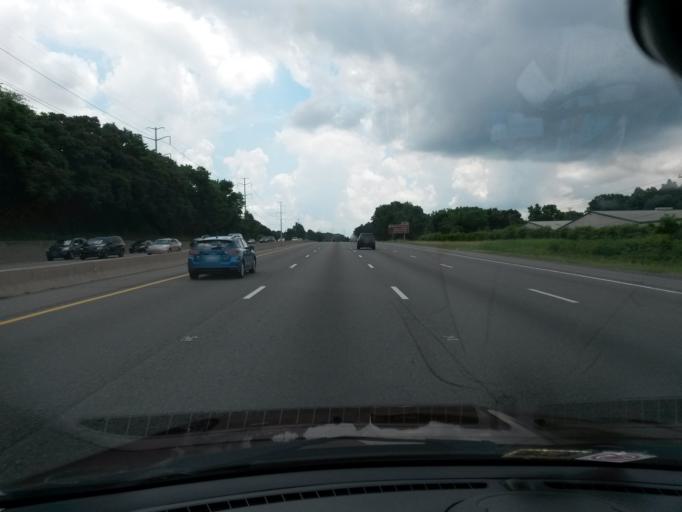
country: US
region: Virginia
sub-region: Chesterfield County
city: Bellwood
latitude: 37.4296
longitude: -77.4308
